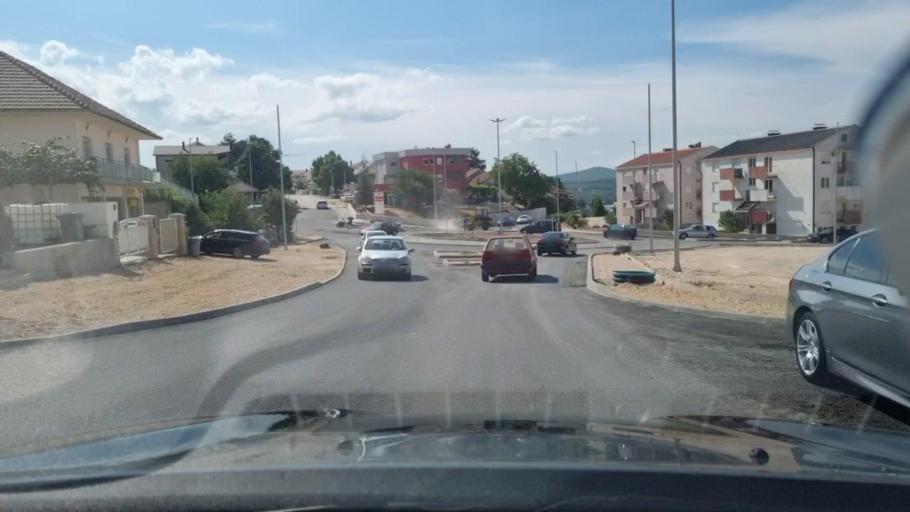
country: BA
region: Federation of Bosnia and Herzegovina
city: Dreznica
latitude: 43.4696
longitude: 17.3230
